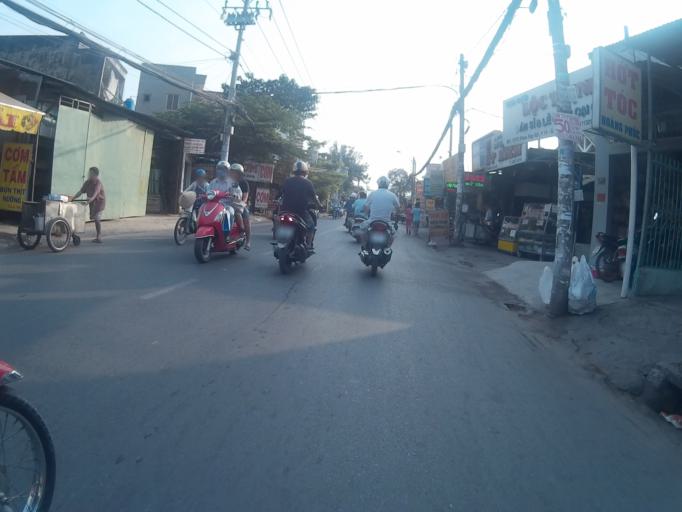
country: VN
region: Ho Chi Minh City
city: Ho Chi Minh City
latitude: 10.8381
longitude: 106.6368
